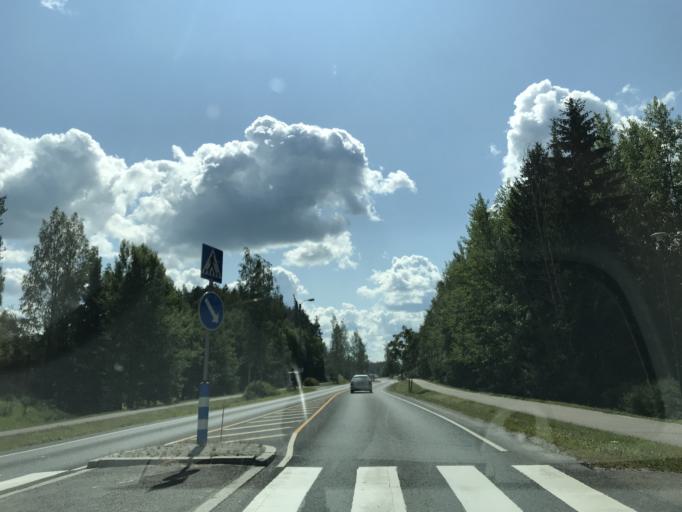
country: FI
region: Paijanne Tavastia
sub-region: Lahti
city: Orimattila
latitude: 60.8172
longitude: 25.7303
